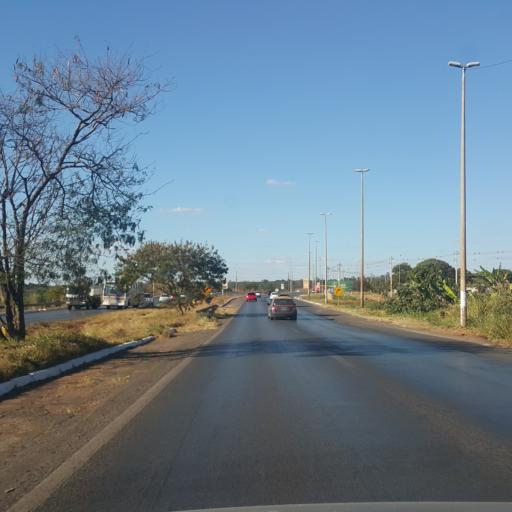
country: BR
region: Federal District
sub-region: Brasilia
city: Brasilia
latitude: -15.8001
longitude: -48.0763
